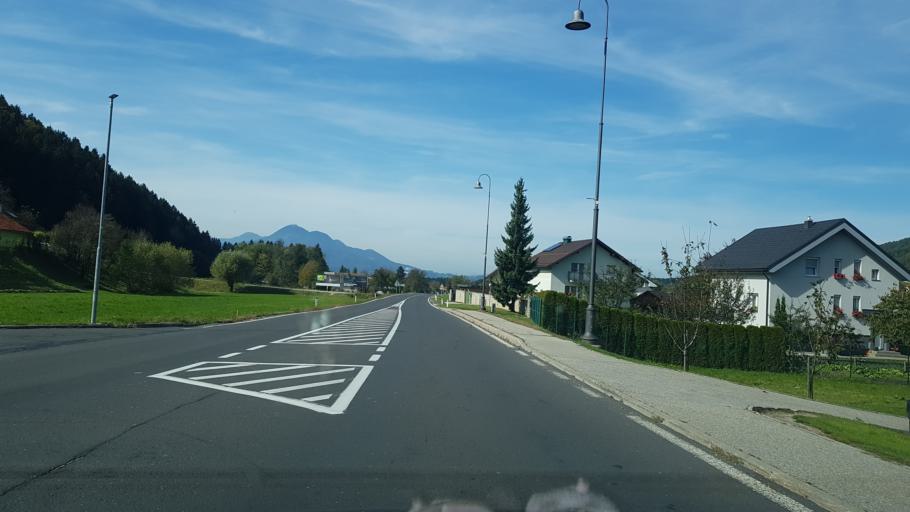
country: SI
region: Mislinja
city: Mislinja
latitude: 46.4434
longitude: 15.1918
